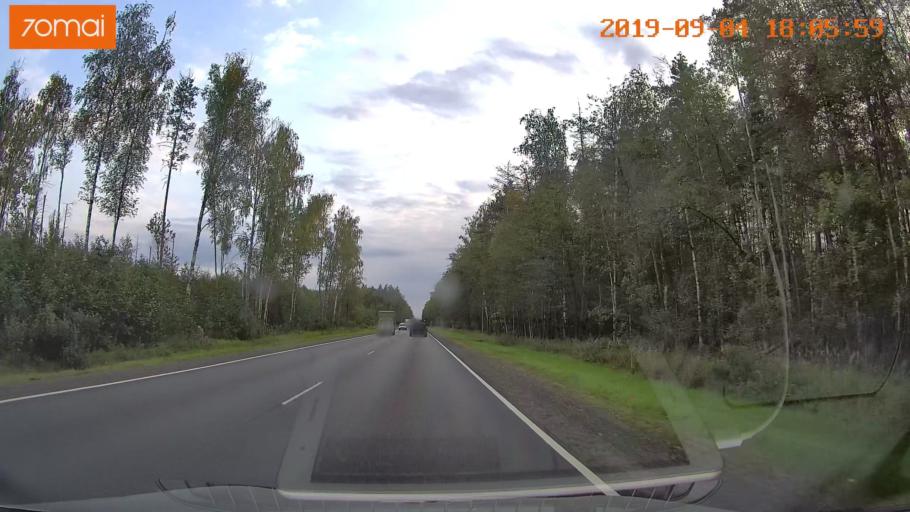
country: RU
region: Moskovskaya
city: Il'inskiy Pogost
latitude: 55.4355
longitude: 38.8199
